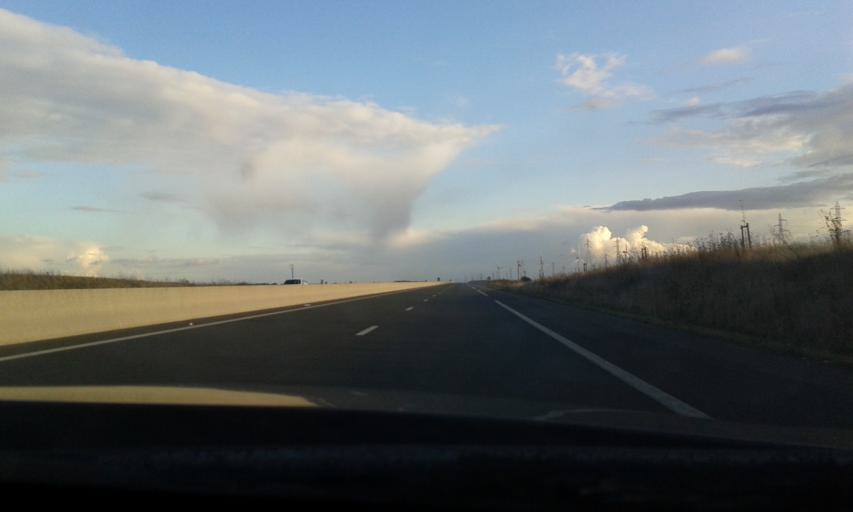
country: FR
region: Centre
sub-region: Departement d'Eure-et-Loir
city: Sours
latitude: 48.3465
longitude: 1.6276
